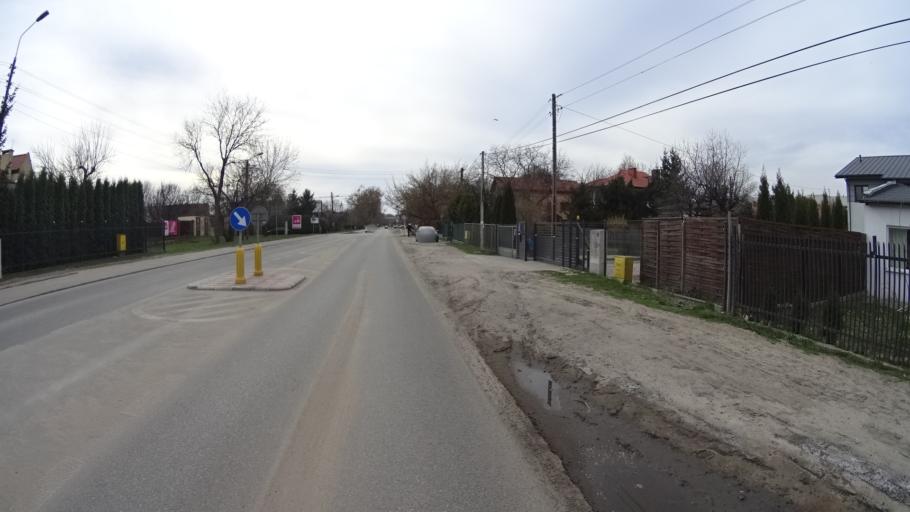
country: PL
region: Masovian Voivodeship
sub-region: Warszawa
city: Praga Poludnie
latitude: 52.2126
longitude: 21.0730
